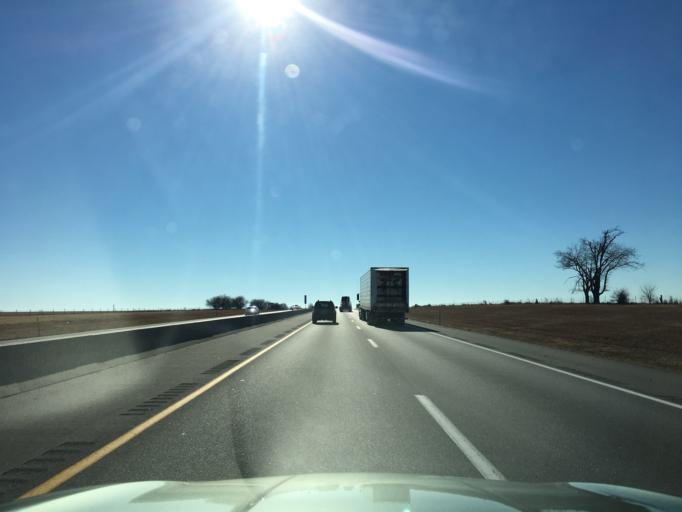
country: US
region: Kansas
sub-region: Sumner County
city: Wellington
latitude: 37.3036
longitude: -97.3405
